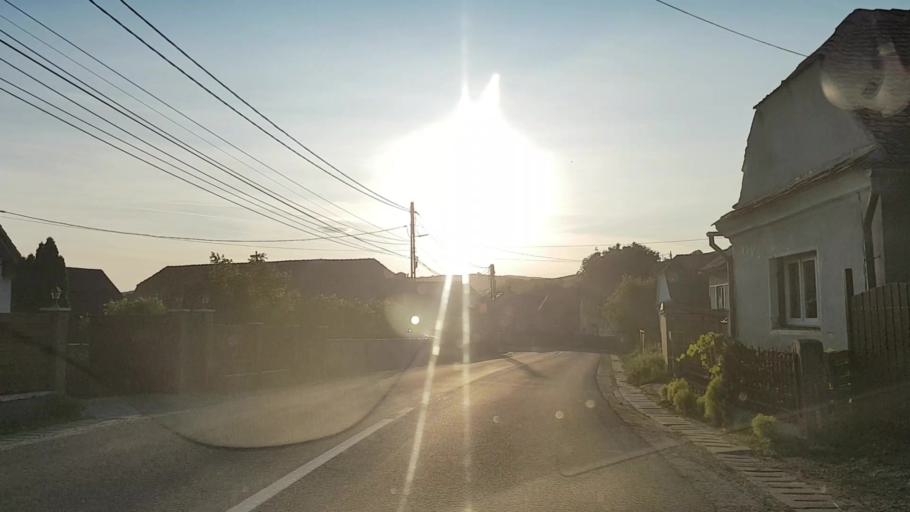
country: RO
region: Harghita
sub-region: Comuna Simonesti
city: Simonesti
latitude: 46.3572
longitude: 25.1511
